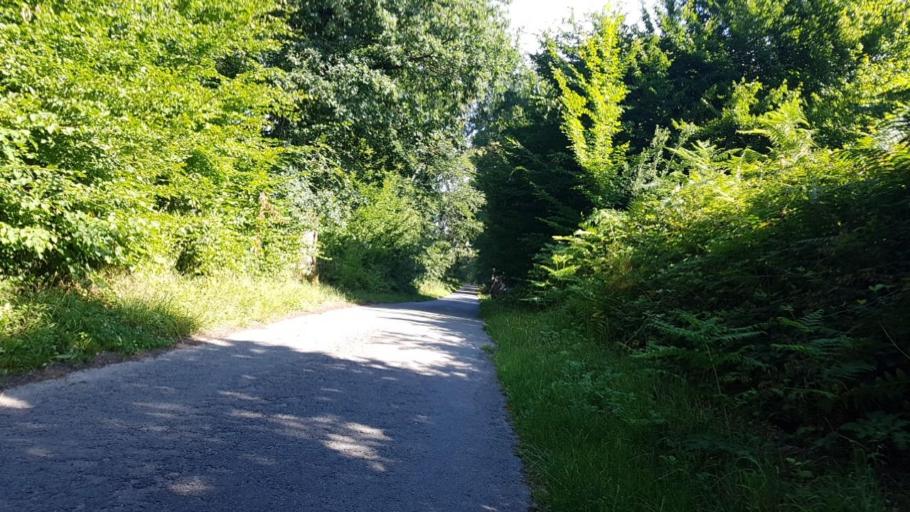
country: FR
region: Picardie
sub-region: Departement de l'Oise
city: Fleurines
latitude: 49.2625
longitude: 2.6187
